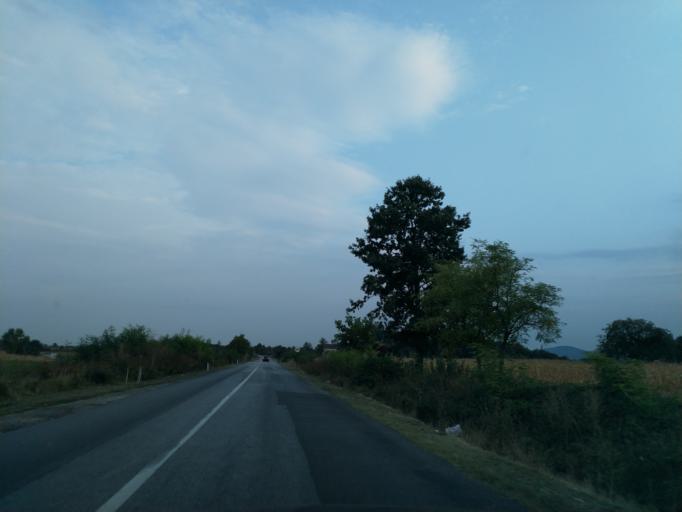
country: RS
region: Central Serbia
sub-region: Sumadijski Okrug
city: Kragujevac
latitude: 44.1136
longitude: 20.8388
